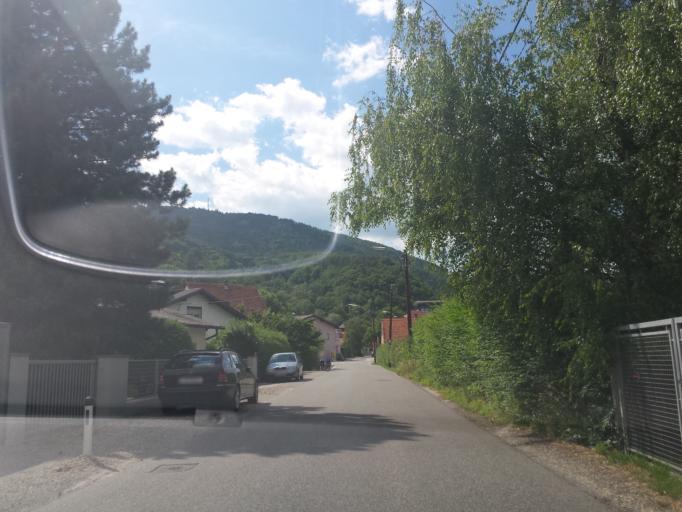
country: AT
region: Styria
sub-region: Graz Stadt
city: Goesting
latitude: 47.0845
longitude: 15.4068
